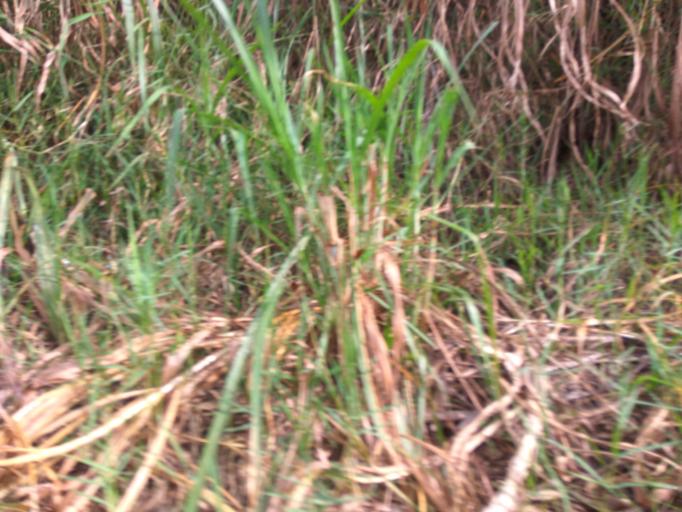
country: TW
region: Taiwan
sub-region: Hsinchu
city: Zhubei
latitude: 24.9810
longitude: 121.0358
